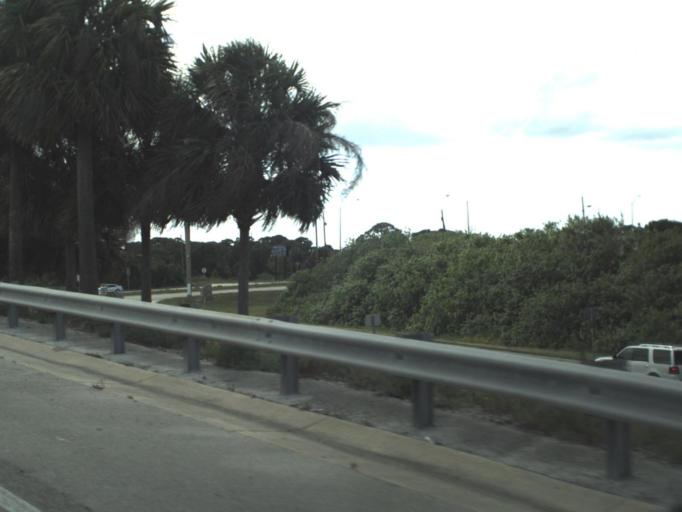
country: US
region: Florida
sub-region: Brevard County
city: Cocoa
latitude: 28.4054
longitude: -80.7045
